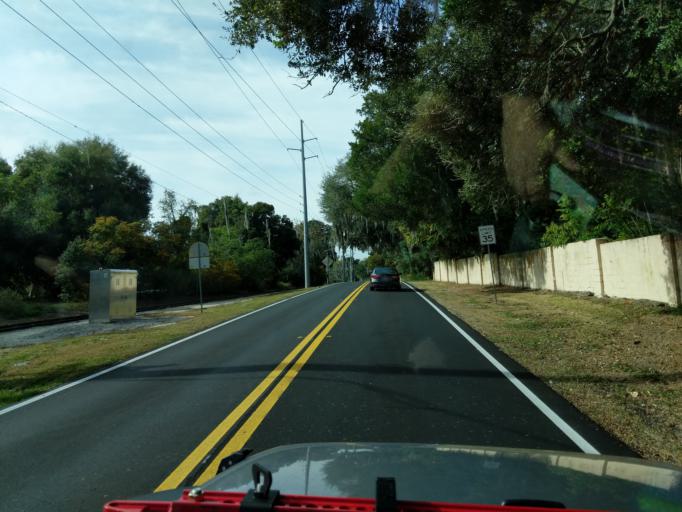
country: US
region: Florida
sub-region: Lake County
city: Mount Dora
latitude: 28.8063
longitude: -81.6577
